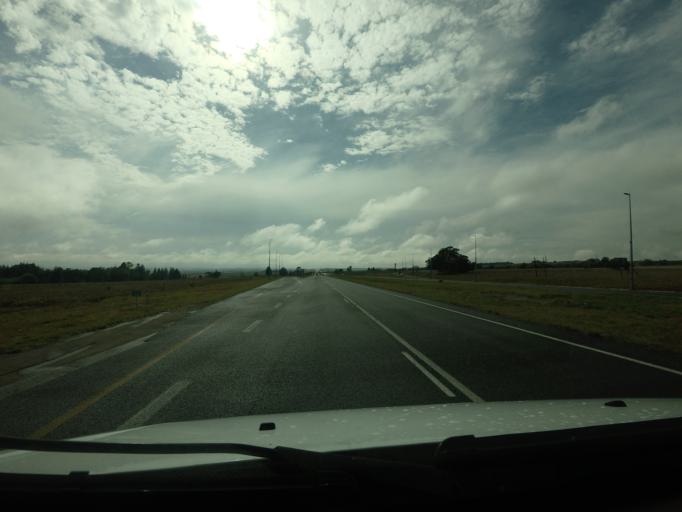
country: ZA
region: Gauteng
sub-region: City of Tshwane Metropolitan Municipality
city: Cullinan
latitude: -25.7972
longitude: 28.5113
